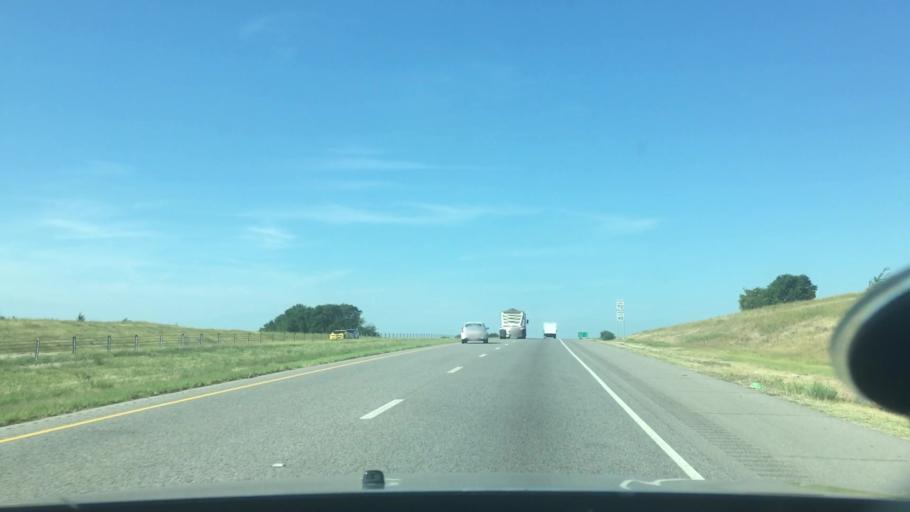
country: US
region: Oklahoma
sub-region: Bryan County
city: Durant
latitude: 34.1255
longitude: -96.2821
